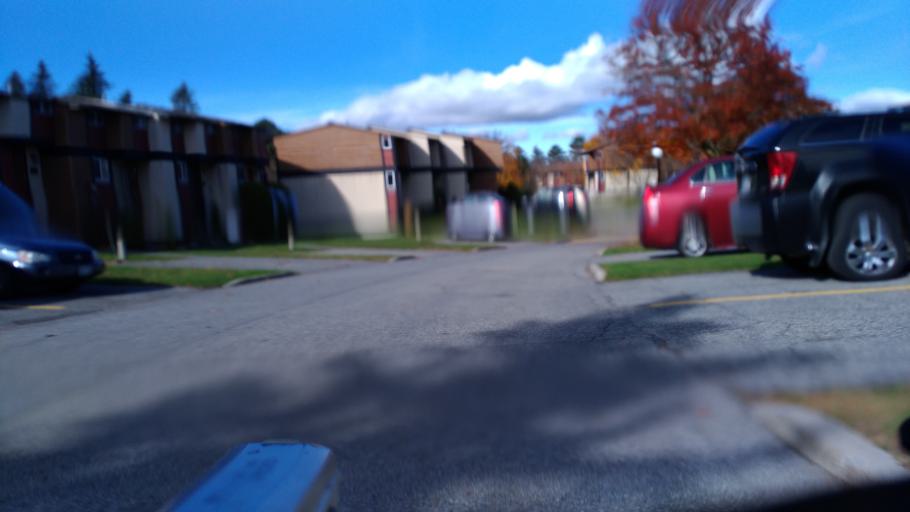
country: CA
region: Ontario
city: Bells Corners
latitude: 45.3078
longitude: -75.8965
